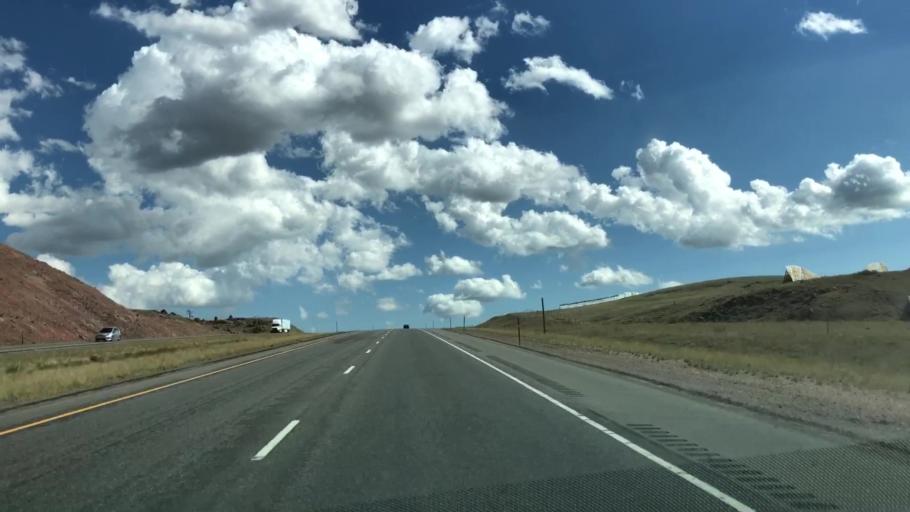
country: US
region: Wyoming
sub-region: Albany County
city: Laramie
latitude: 41.0580
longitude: -105.4730
